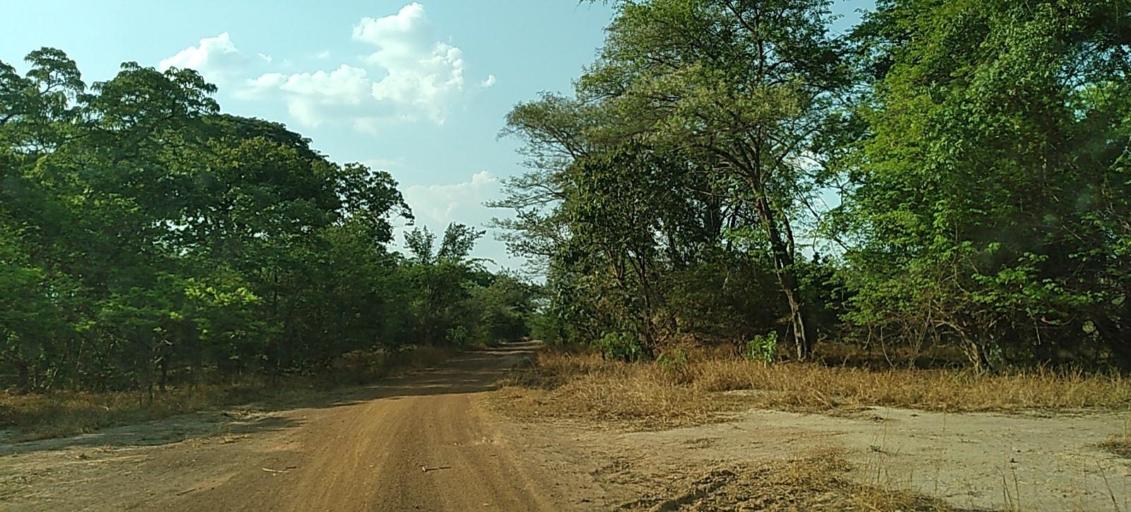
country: ZM
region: Copperbelt
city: Mpongwe
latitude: -13.4447
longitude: 28.0627
